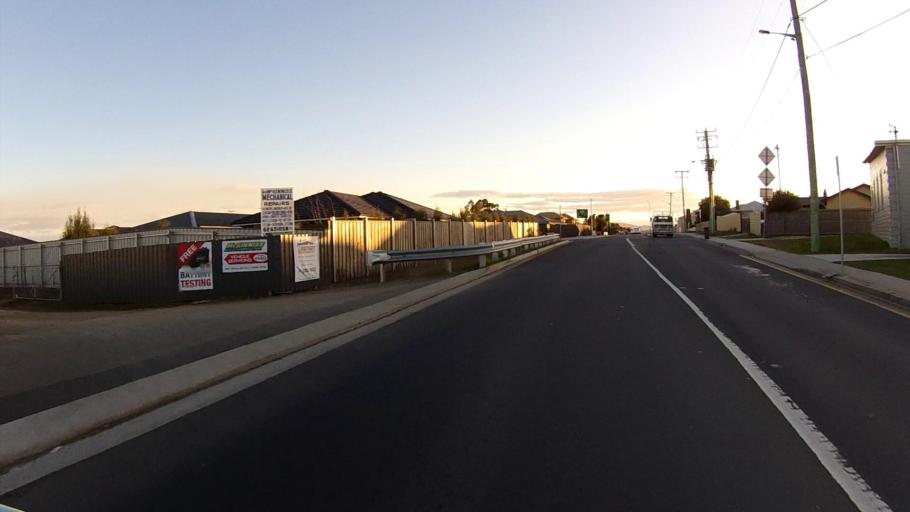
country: AU
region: Tasmania
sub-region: Sorell
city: Sorell
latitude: -42.7863
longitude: 147.5636
